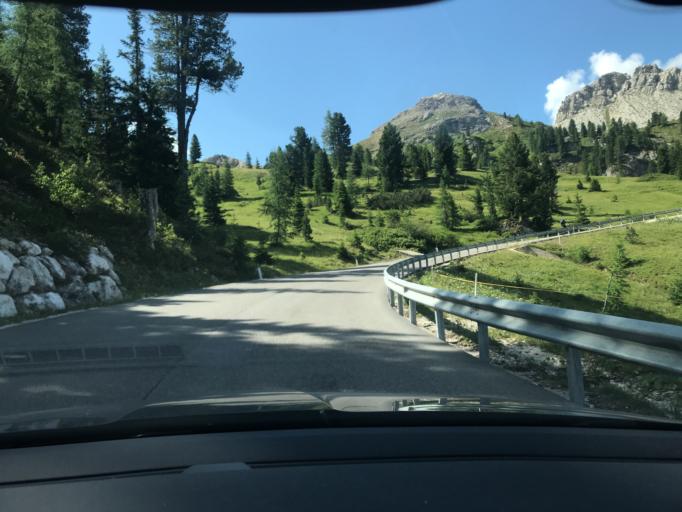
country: IT
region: Veneto
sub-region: Provincia di Belluno
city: Livinallongo del Col di Lana
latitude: 46.5363
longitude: 11.9855
